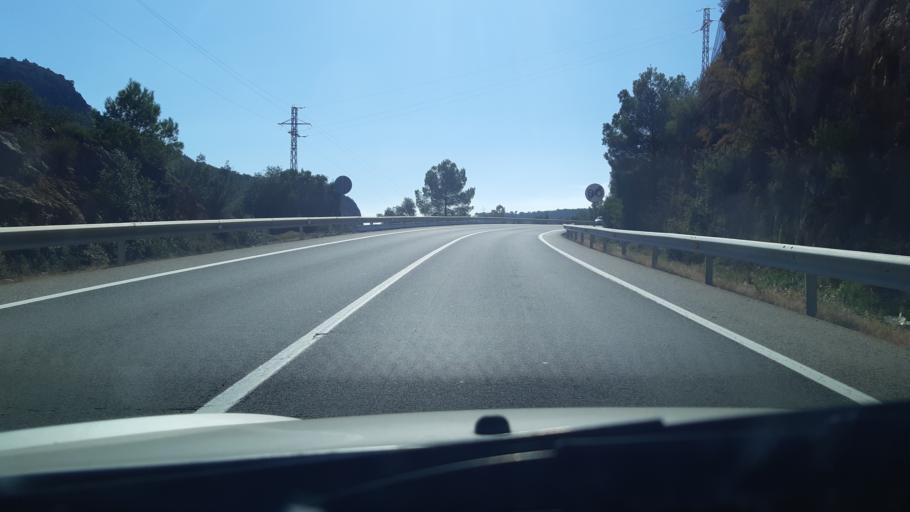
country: ES
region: Catalonia
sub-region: Provincia de Tarragona
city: Tivenys
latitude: 40.9392
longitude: 0.4887
